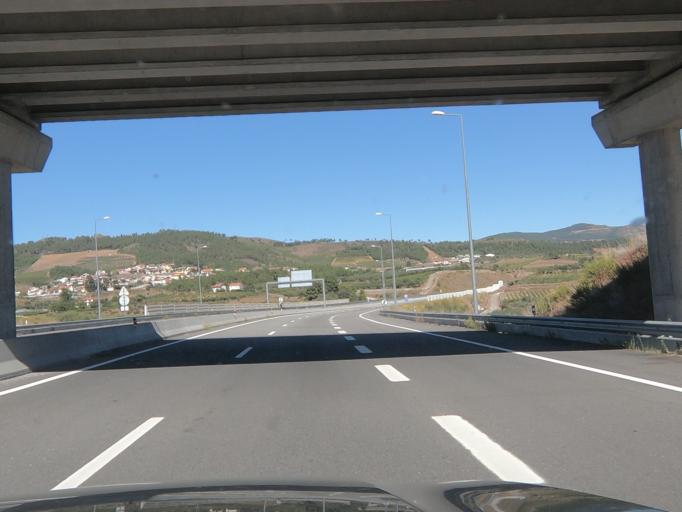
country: PT
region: Vila Real
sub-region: Murca
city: Murca
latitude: 41.3973
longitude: -7.4450
